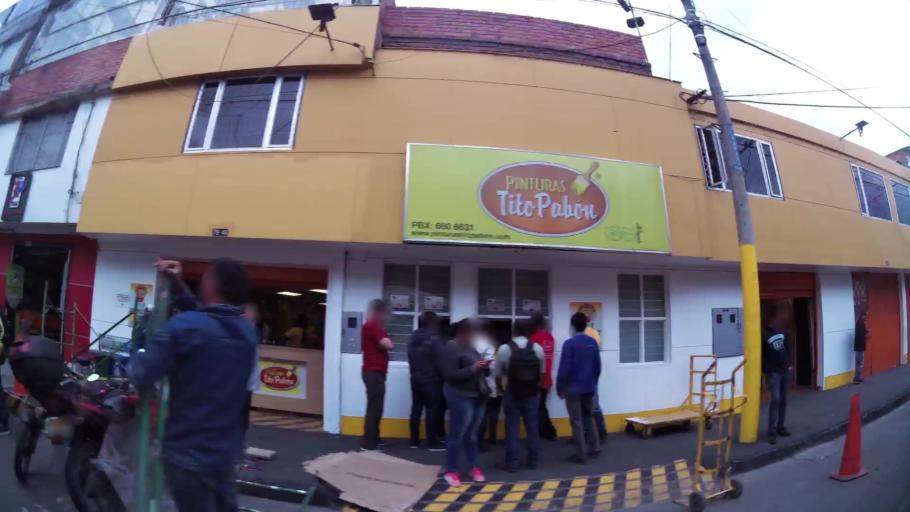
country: CO
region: Bogota D.C.
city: Barrio San Luis
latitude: 4.6692
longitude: -74.0649
